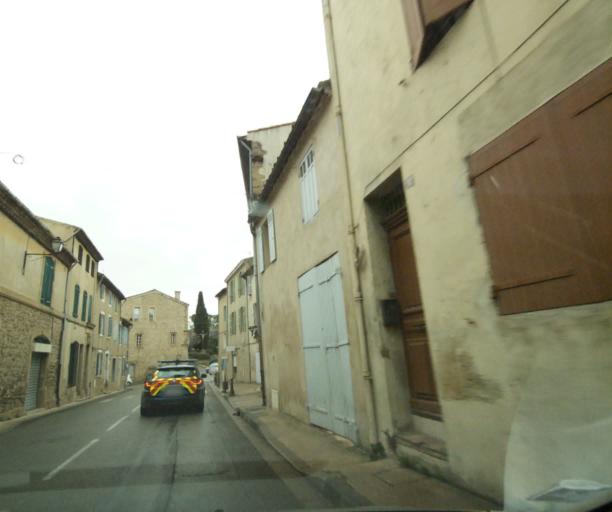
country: FR
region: Provence-Alpes-Cote d'Azur
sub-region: Departement des Bouches-du-Rhone
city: Rognes
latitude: 43.6635
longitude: 5.3482
